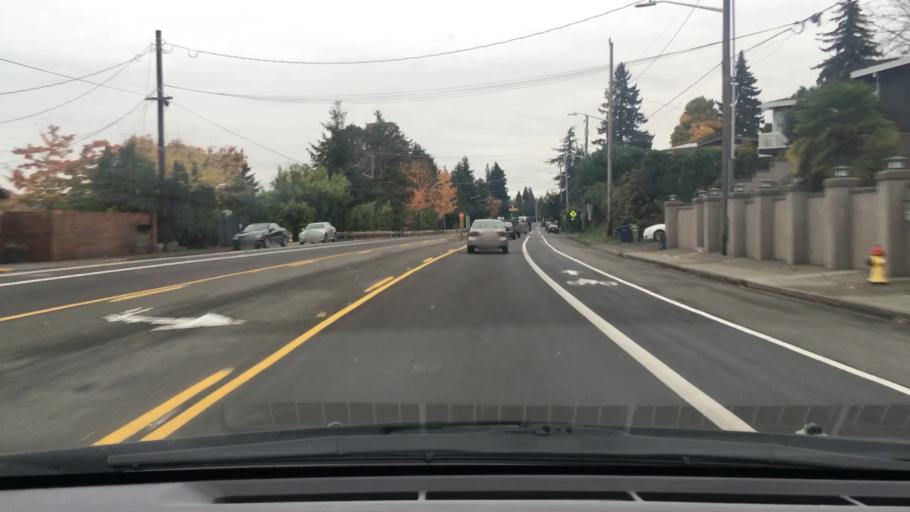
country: US
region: Washington
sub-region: King County
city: Bryn Mawr-Skyway
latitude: 47.5033
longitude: -122.2254
